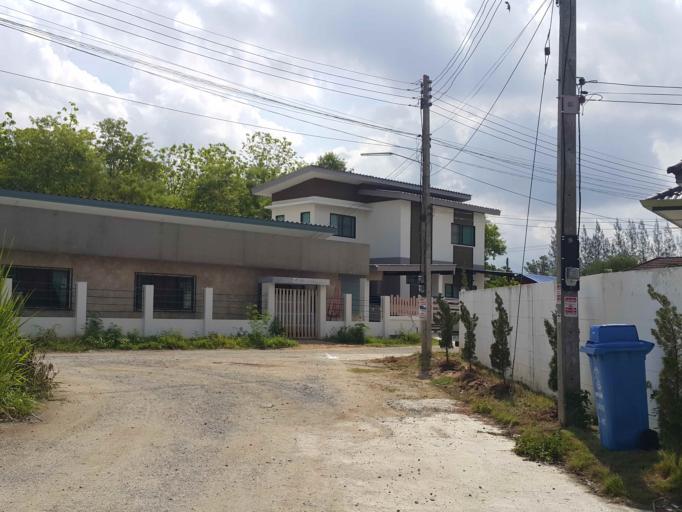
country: TH
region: Chiang Mai
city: San Kamphaeng
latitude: 18.7670
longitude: 99.0690
